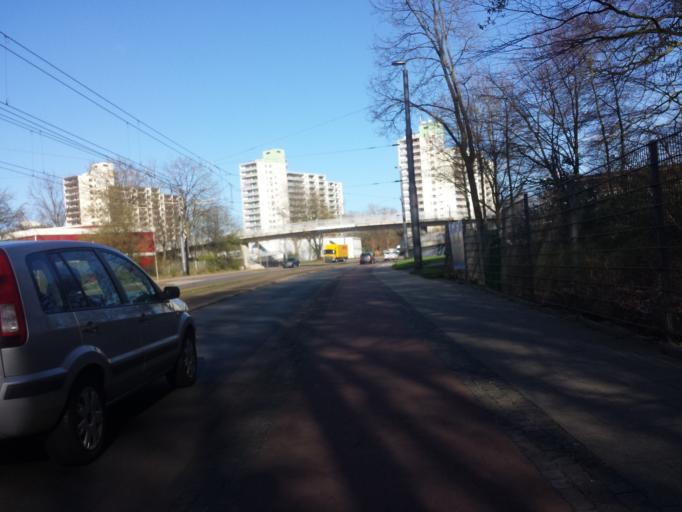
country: DE
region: Lower Saxony
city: Oyten
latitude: 53.0666
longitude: 8.9582
